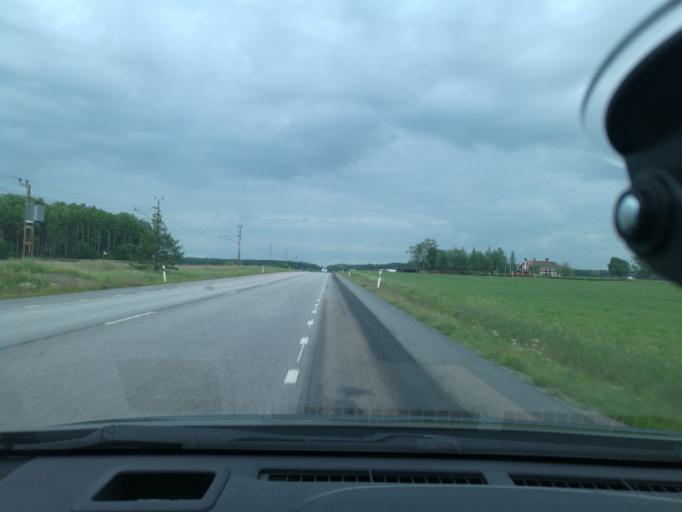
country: SE
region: Vaestmanland
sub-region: Sala Kommun
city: Sala
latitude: 59.9262
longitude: 16.6745
